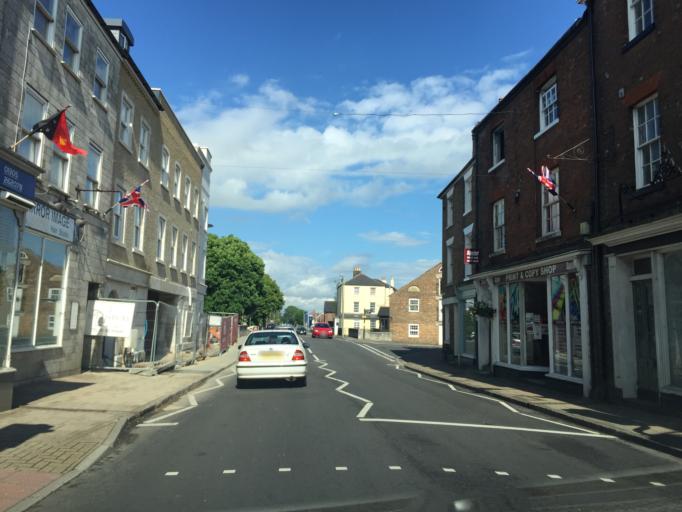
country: GB
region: England
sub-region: Dorset
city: Dorchester
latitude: 50.7157
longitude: -2.4335
